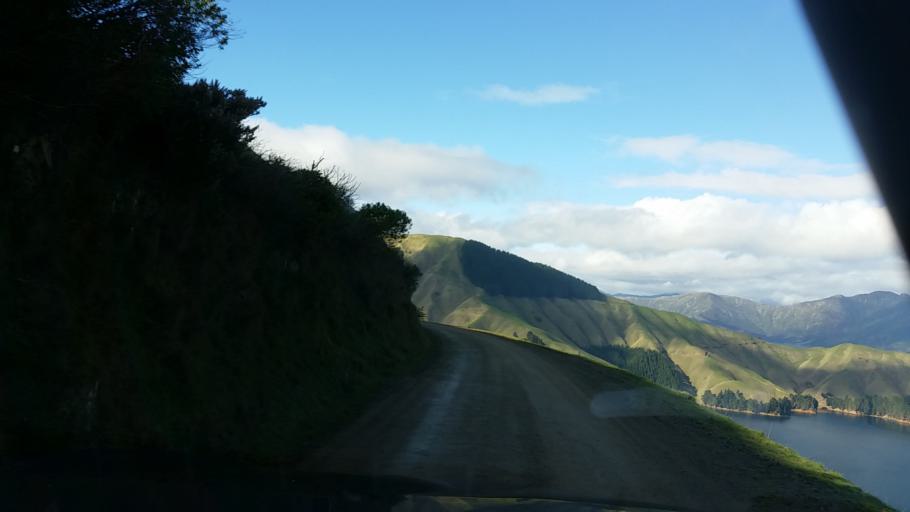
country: NZ
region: Marlborough
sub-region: Marlborough District
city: Picton
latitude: -40.9869
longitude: 173.8130
